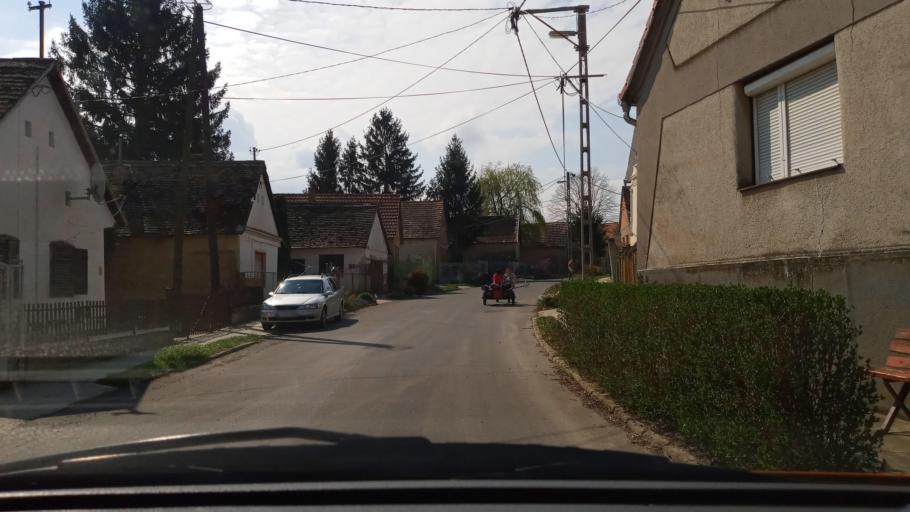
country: HU
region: Baranya
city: Pecsvarad
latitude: 46.1006
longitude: 18.4727
